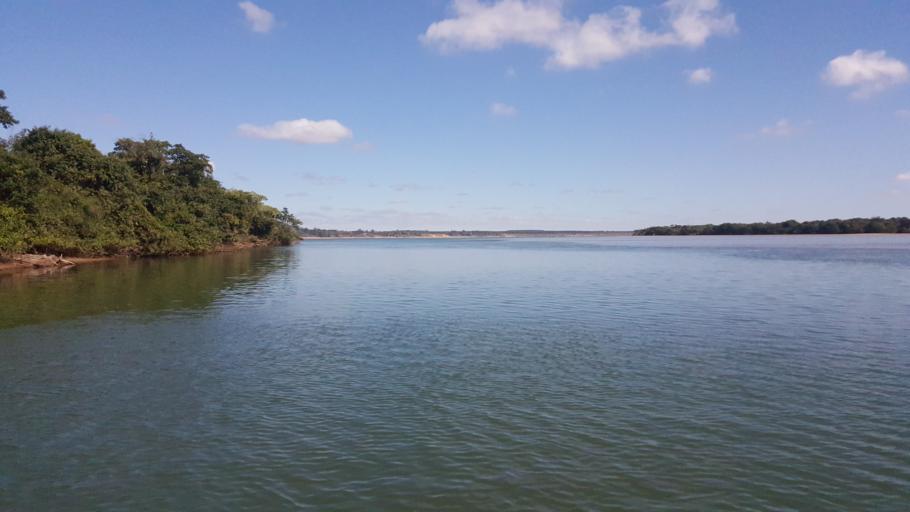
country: AR
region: Corrientes
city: Ituzaingo
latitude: -27.5801
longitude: -56.7106
